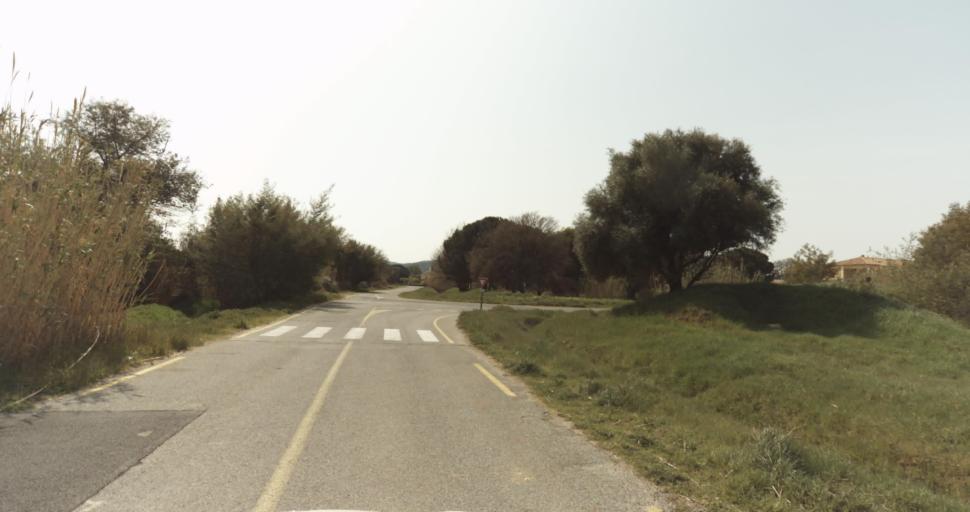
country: FR
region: Provence-Alpes-Cote d'Azur
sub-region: Departement du Var
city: Bormes-les-Mimosas
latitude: 43.1375
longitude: 6.3493
